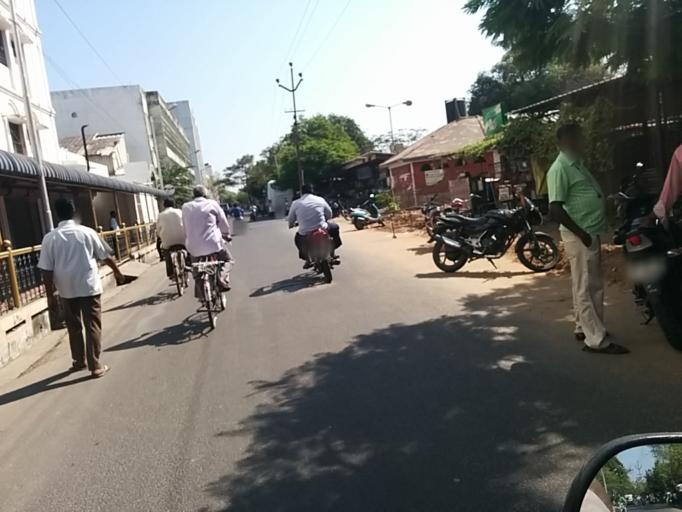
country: IN
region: Pondicherry
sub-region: Puducherry
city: Puducherry
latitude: 11.9337
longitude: 79.8326
